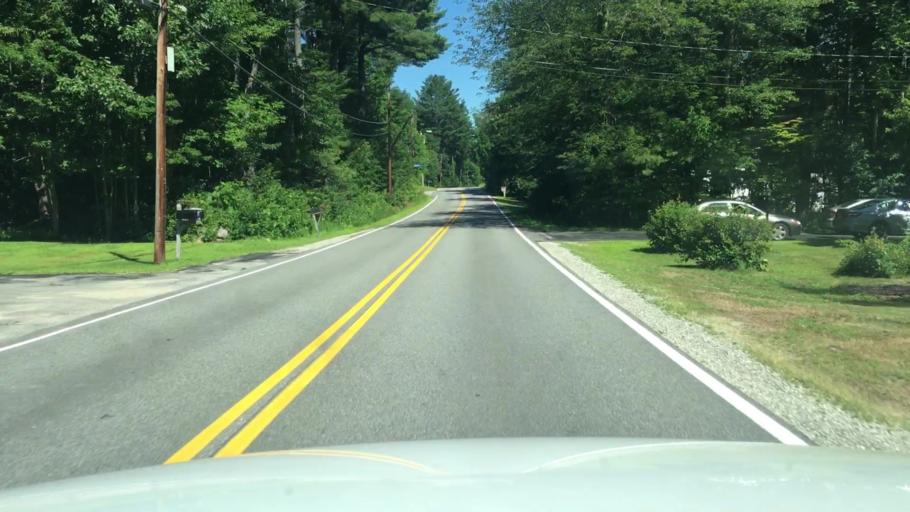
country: US
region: New Hampshire
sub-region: Merrimack County
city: South Hooksett
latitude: 43.0404
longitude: -71.4175
